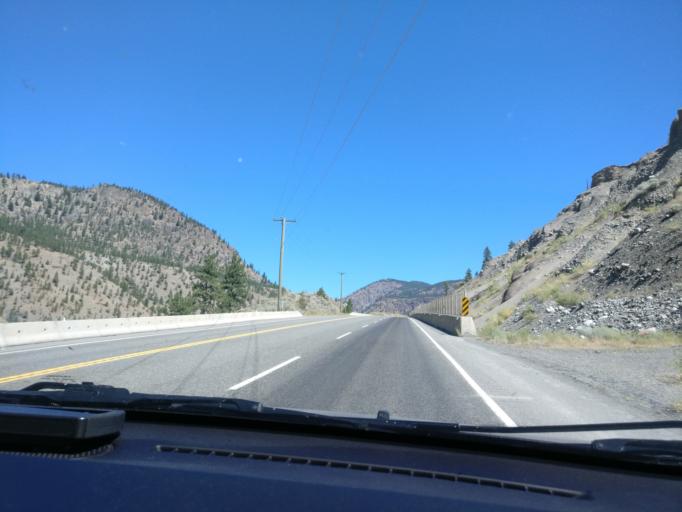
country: CA
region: British Columbia
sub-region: Thompson-Nicola Regional District
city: Ashcroft
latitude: 50.2835
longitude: -121.4029
